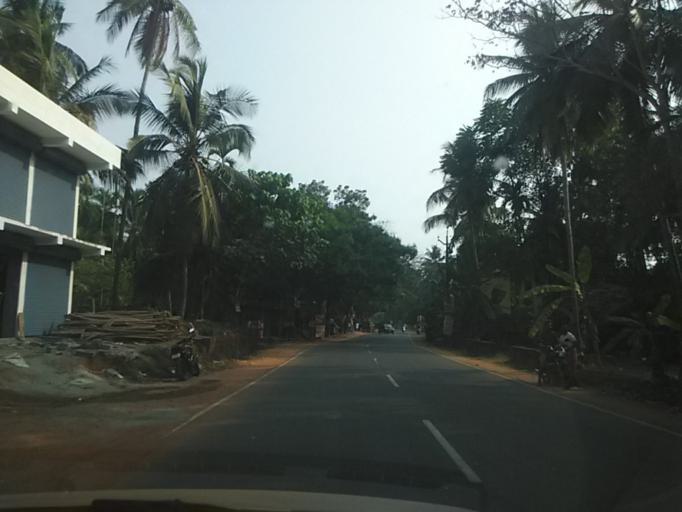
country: IN
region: Kerala
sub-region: Kozhikode
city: Naduvannur
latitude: 11.4818
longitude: 75.7748
